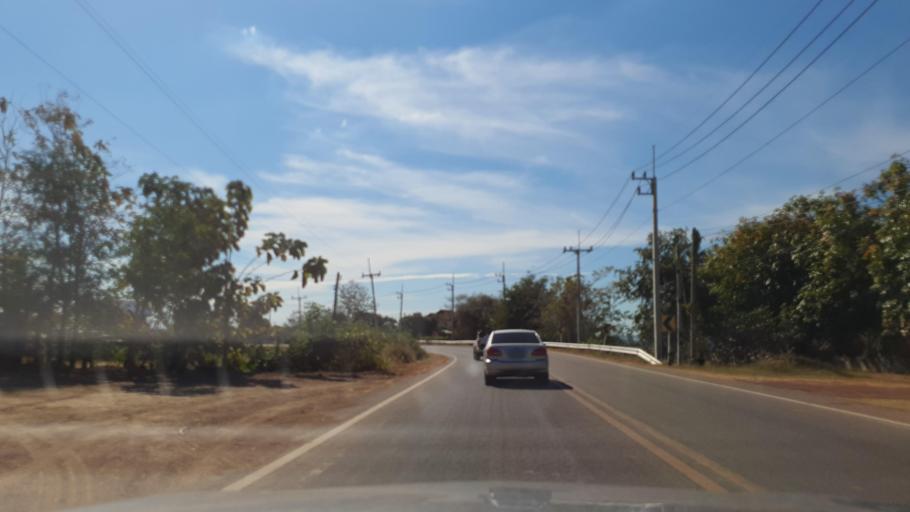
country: TH
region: Kalasin
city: Khao Wong
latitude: 16.7417
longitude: 104.1076
